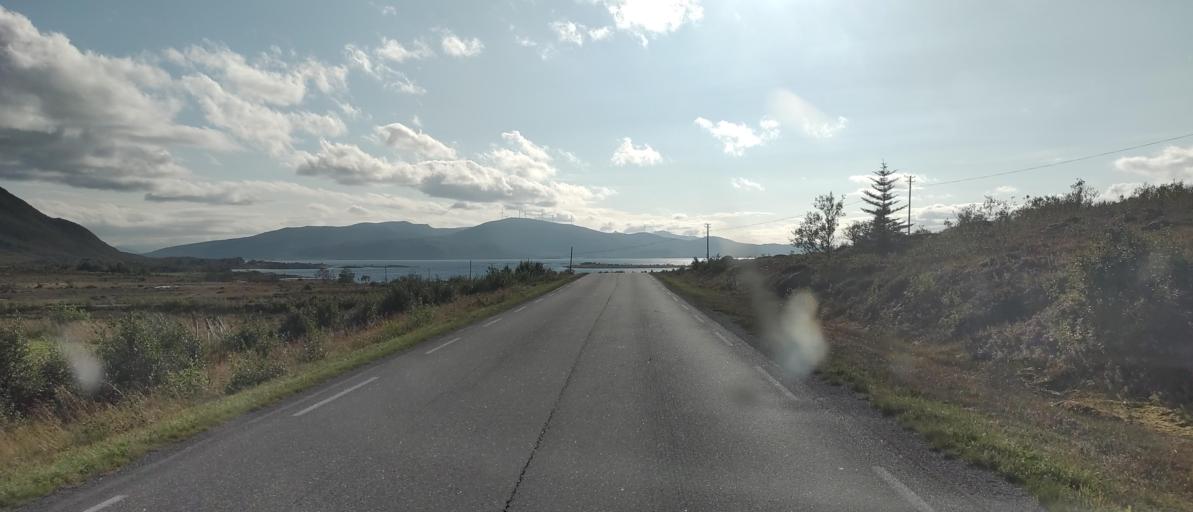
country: NO
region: Nordland
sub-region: Sortland
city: Sortland
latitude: 68.7885
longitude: 15.4961
